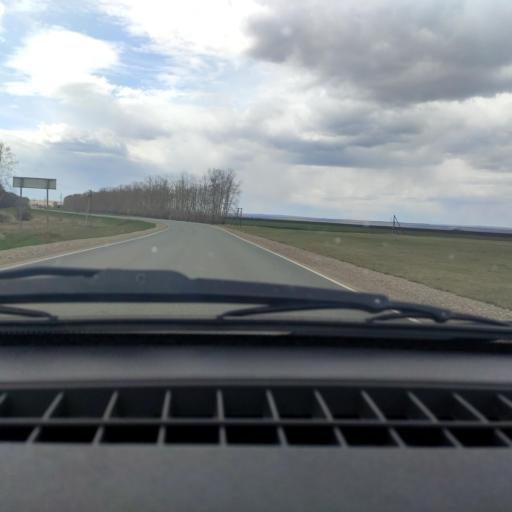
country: RU
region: Bashkortostan
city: Kushnarenkovo
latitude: 55.0580
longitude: 55.1623
